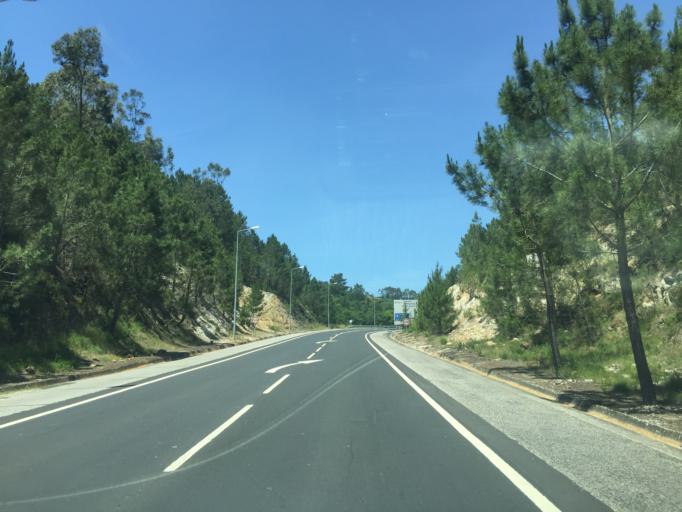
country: PT
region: Lisbon
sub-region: Mafra
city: Venda do Pinheiro
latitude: 38.8986
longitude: -9.2039
